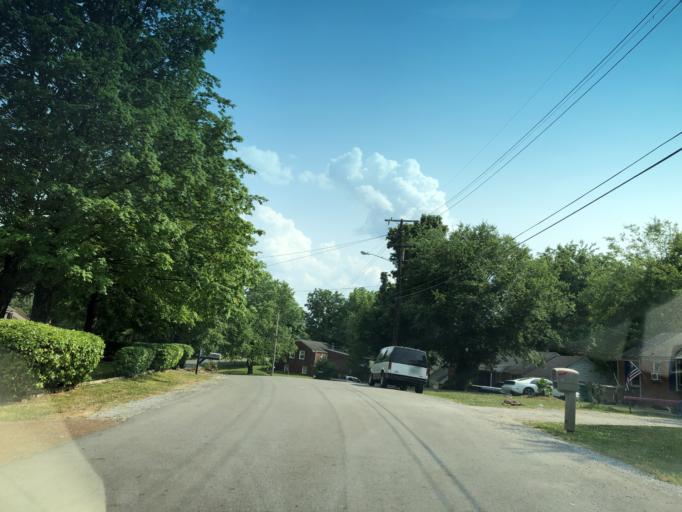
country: US
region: Tennessee
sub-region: Davidson County
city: Goodlettsville
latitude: 36.2544
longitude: -86.7232
